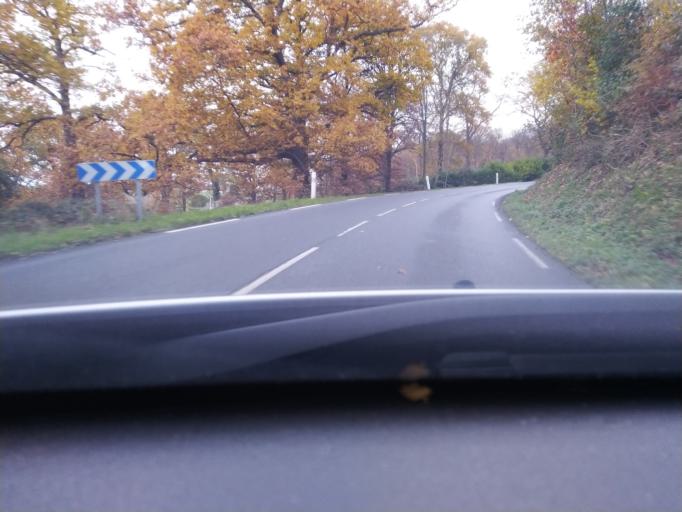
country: FR
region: Haute-Normandie
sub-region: Departement de la Seine-Maritime
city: Duclair
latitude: 49.4889
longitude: 0.8876
